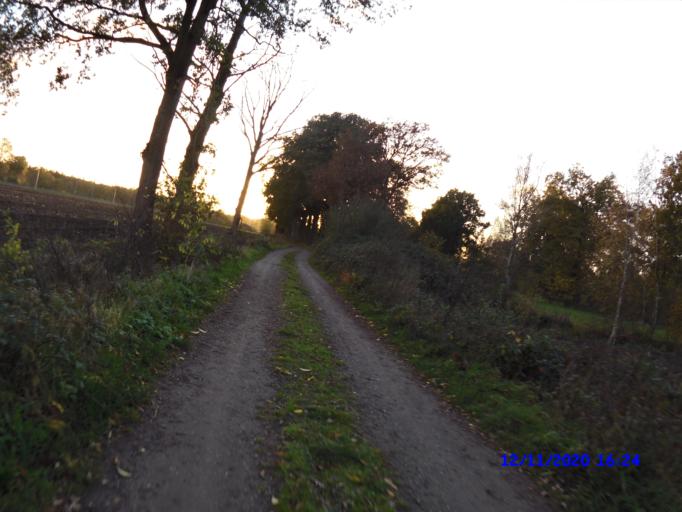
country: BE
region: Flanders
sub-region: Provincie Antwerpen
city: Meerhout
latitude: 51.1817
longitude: 5.0569
